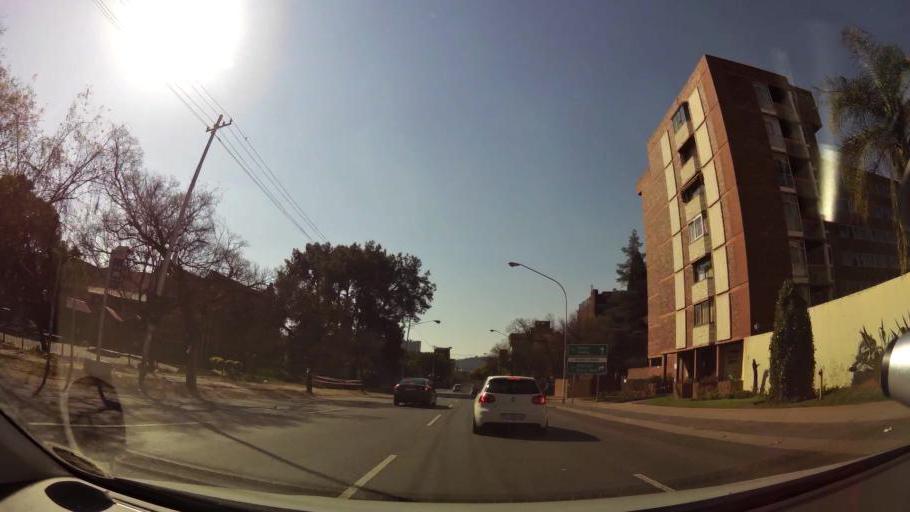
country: ZA
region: Gauteng
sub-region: City of Tshwane Metropolitan Municipality
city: Pretoria
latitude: -25.7571
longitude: 28.2007
